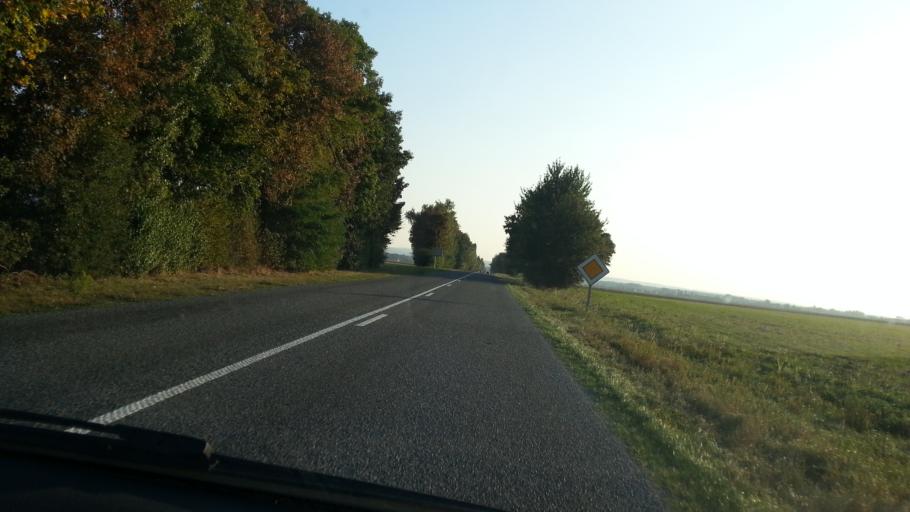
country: FR
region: Picardie
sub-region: Departement de l'Oise
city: Saint-Martin-Longueau
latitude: 49.3606
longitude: 2.6123
